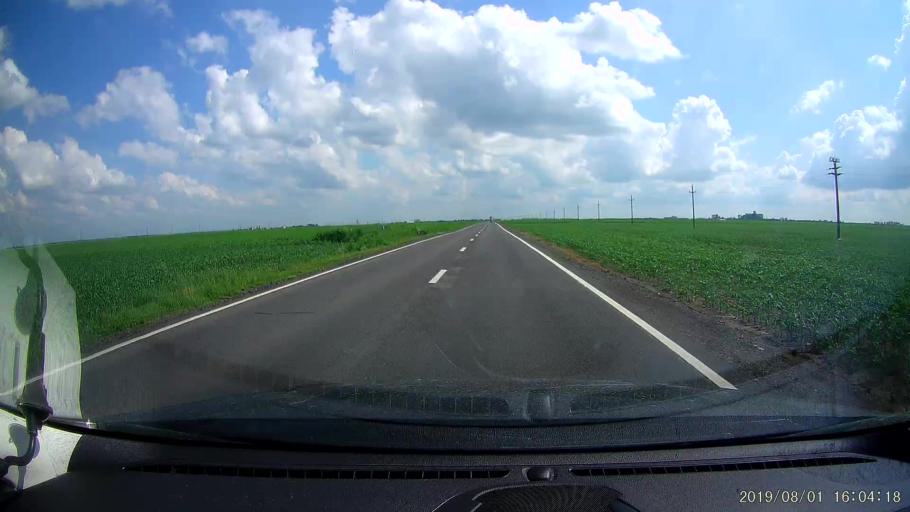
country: RO
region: Calarasi
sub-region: Comuna Dragalina
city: Drajna Noua
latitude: 44.4512
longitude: 27.3807
